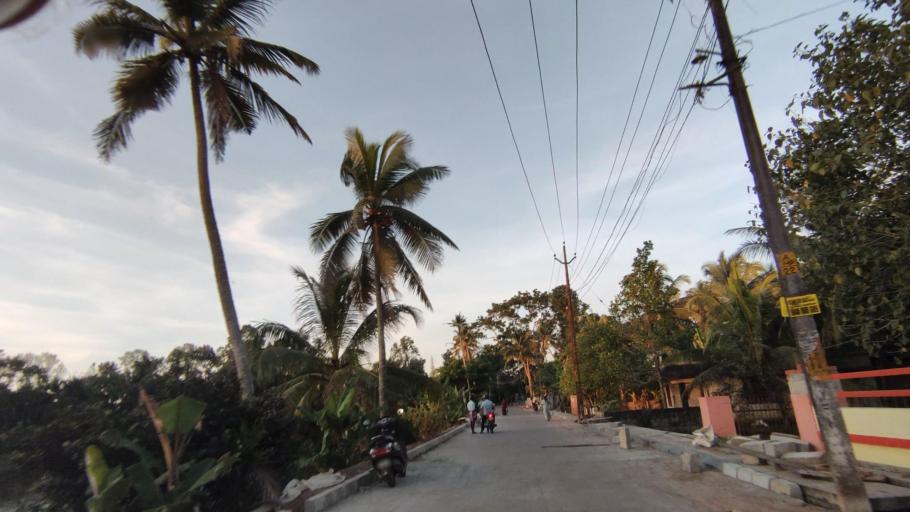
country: IN
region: Kerala
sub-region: Kottayam
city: Kottayam
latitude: 9.6304
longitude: 76.4945
